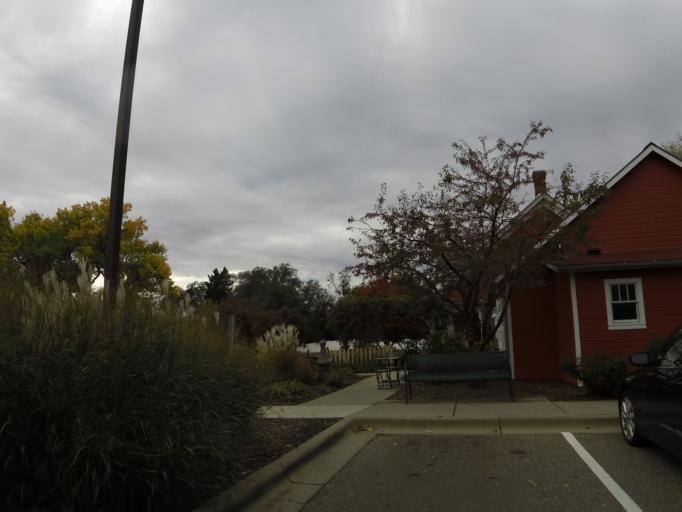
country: US
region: Minnesota
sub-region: Hennepin County
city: Eden Prairie
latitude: 44.8570
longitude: -93.4845
